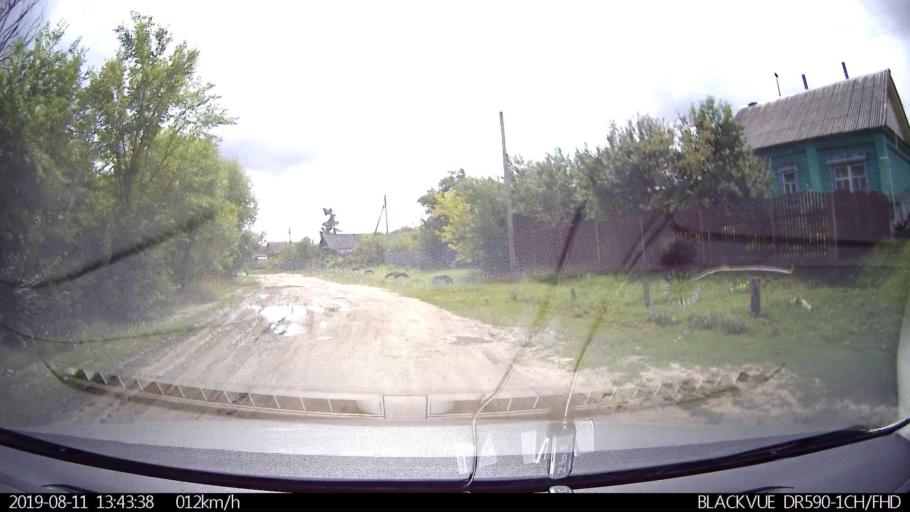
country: RU
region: Ulyanovsk
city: Ignatovka
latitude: 53.8543
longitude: 47.5744
